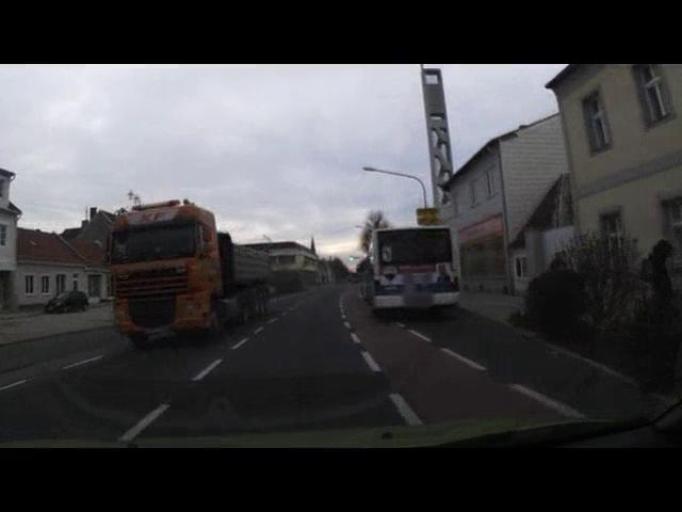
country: AT
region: Burgenland
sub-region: Eisenstadt-Umgebung
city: Neufeld an der Leitha
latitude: 47.8692
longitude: 16.3764
